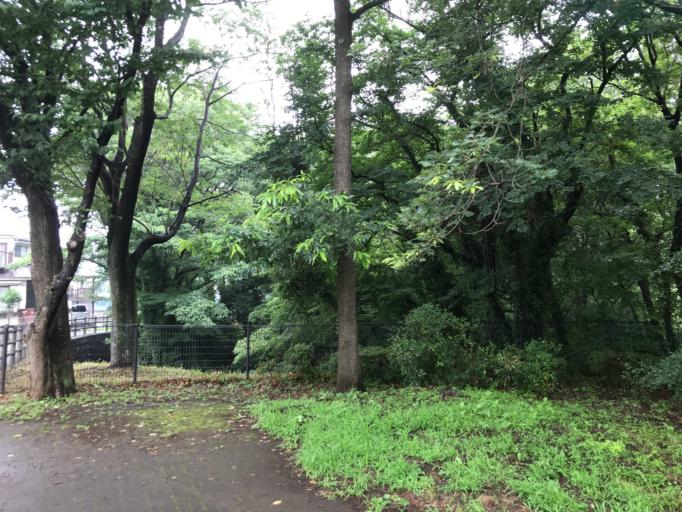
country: JP
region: Tokyo
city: Hachioji
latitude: 35.6744
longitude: 139.3381
